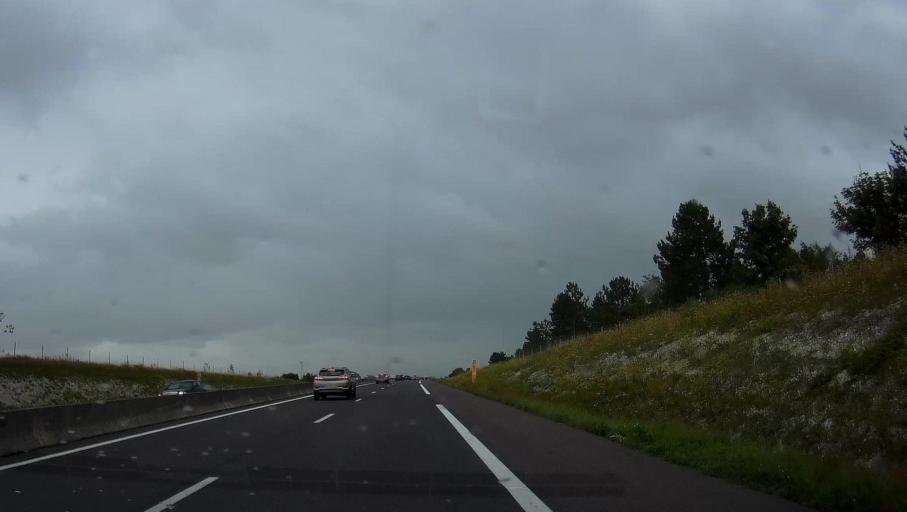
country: FR
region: Champagne-Ardenne
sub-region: Departement de l'Aube
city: Mailly-le-Camp
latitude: 48.6545
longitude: 4.1749
